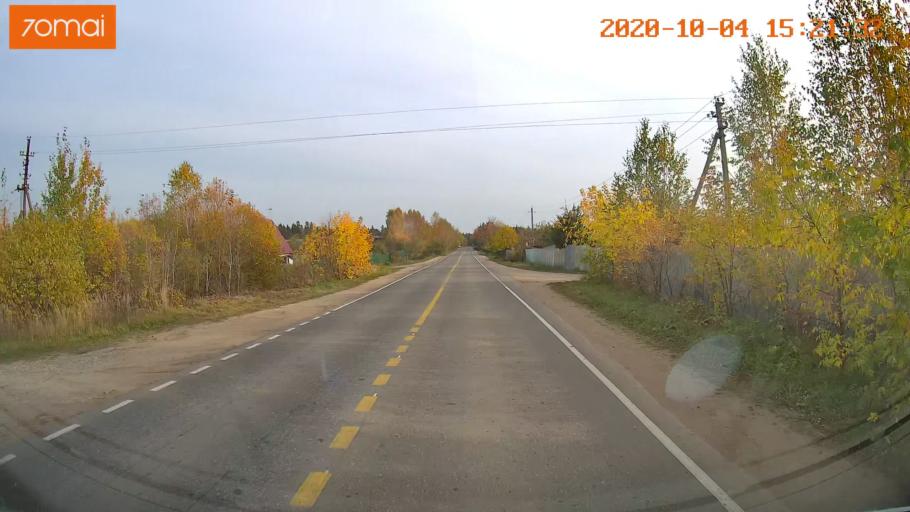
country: RU
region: Ivanovo
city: Bogorodskoye
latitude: 57.0859
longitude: 40.9238
